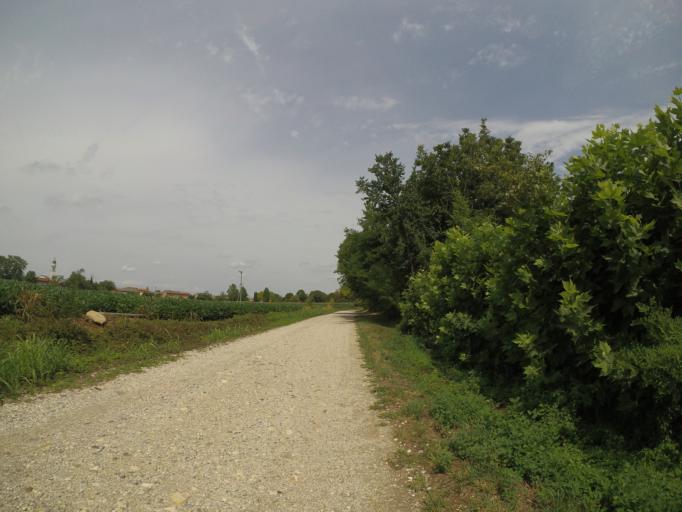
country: IT
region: Friuli Venezia Giulia
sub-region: Provincia di Udine
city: Lestizza
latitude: 45.9622
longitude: 13.1150
